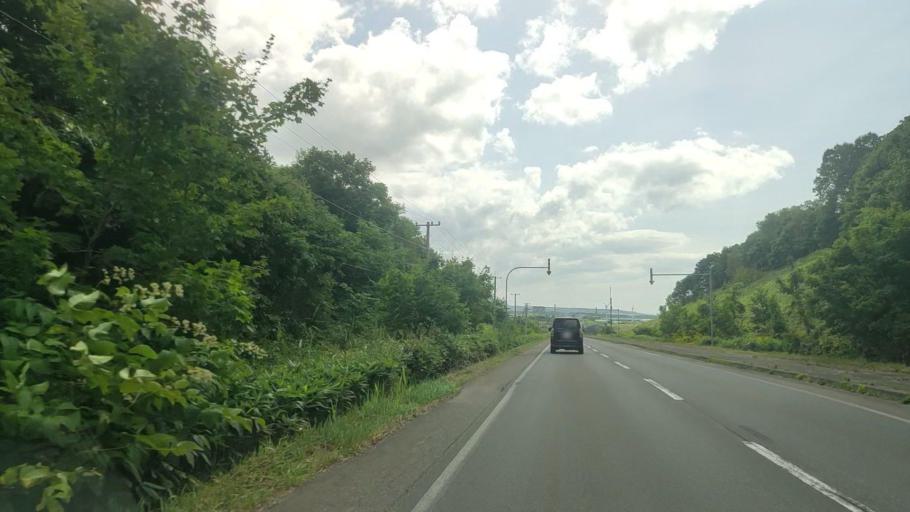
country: JP
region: Hokkaido
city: Makubetsu
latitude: 44.7631
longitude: 141.7937
